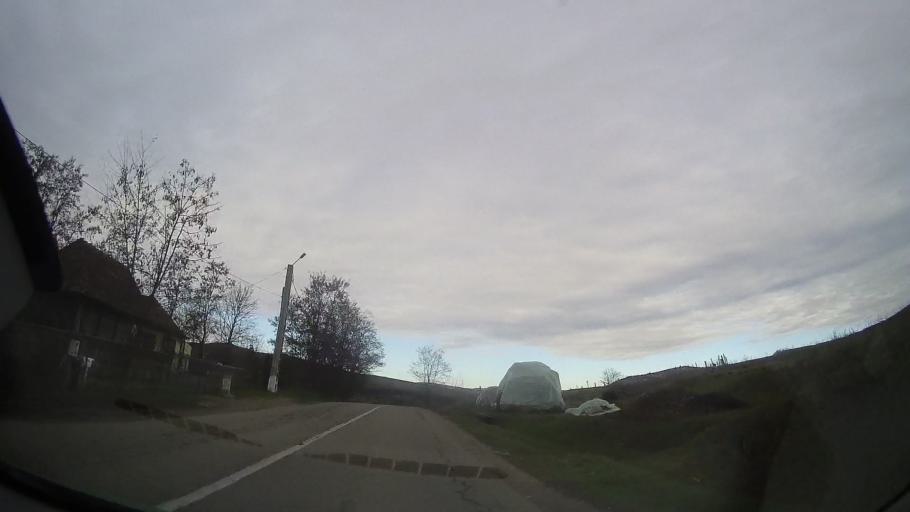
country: RO
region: Cluj
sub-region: Comuna Camarasu
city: Camarasu
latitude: 46.8146
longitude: 24.1409
